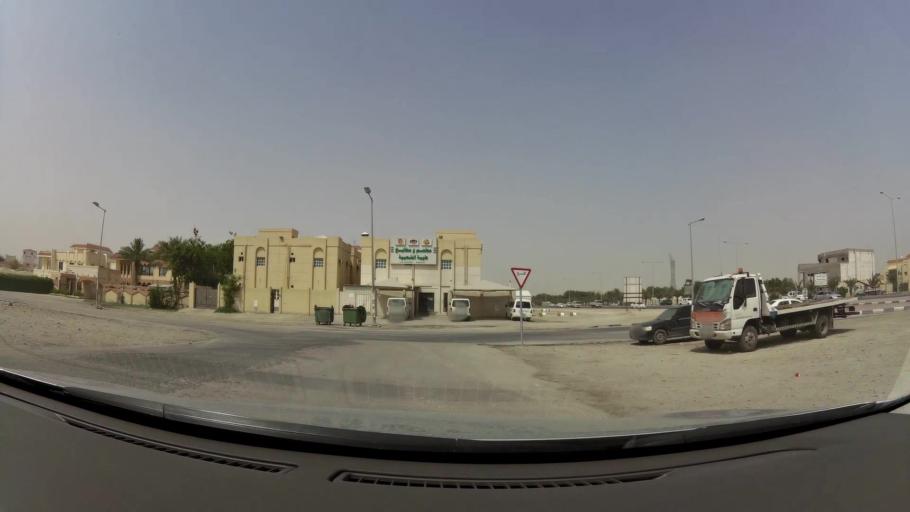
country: QA
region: Baladiyat ar Rayyan
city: Ar Rayyan
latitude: 25.2404
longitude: 51.4307
